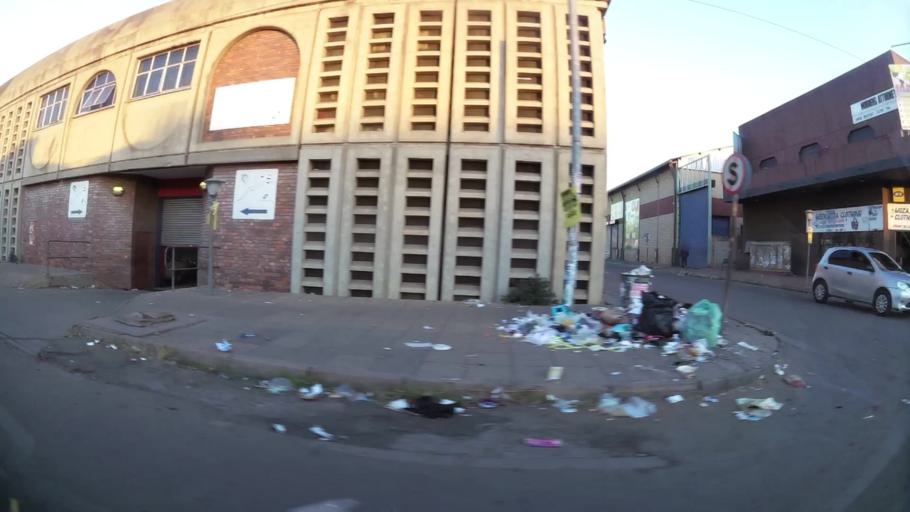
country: ZA
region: North-West
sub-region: Bojanala Platinum District Municipality
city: Rustenburg
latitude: -25.6690
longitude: 27.2411
